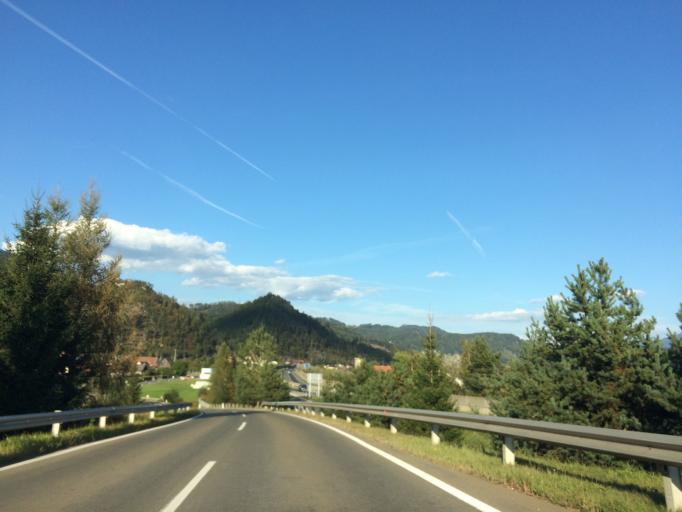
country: AT
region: Styria
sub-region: Politischer Bezirk Leoben
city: Sankt Michael in Obersteiermark
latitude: 47.3272
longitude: 14.9732
